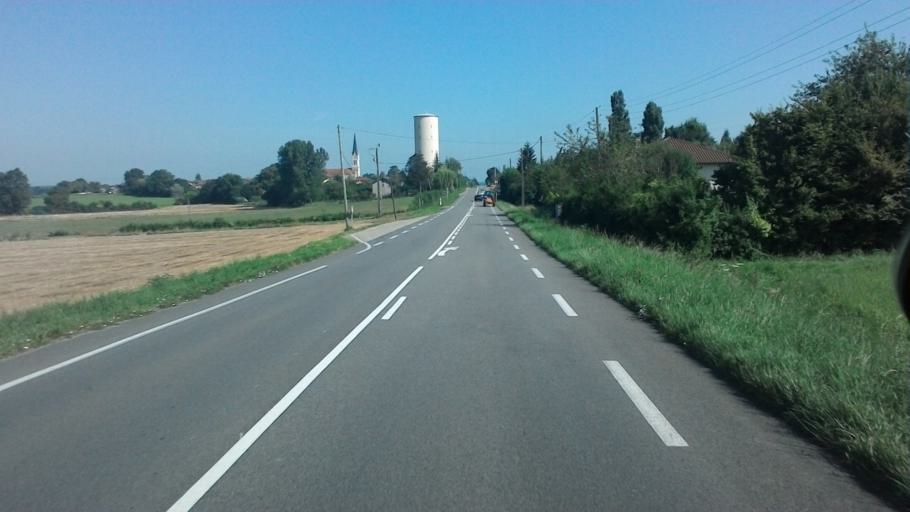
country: FR
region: Rhone-Alpes
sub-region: Departement de l'Ain
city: Montrevel-en-Bresse
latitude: 46.3632
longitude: 5.1221
